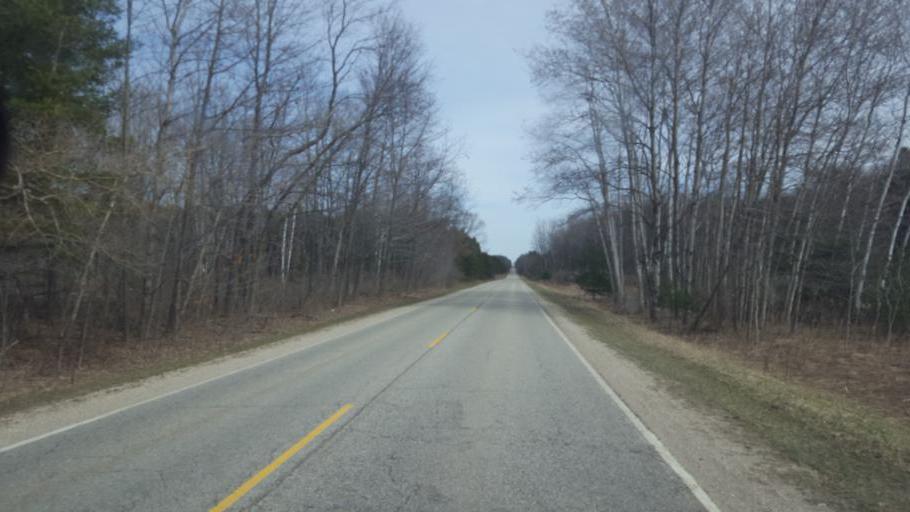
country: US
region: Michigan
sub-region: Isabella County
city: Lake Isabella
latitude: 43.6611
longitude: -85.1036
